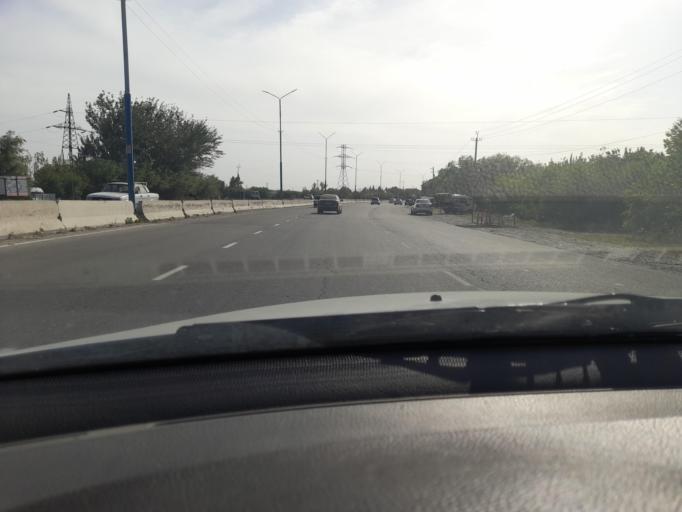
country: UZ
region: Samarqand
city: Kattaqo'rg'on
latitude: 39.9231
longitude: 66.2372
